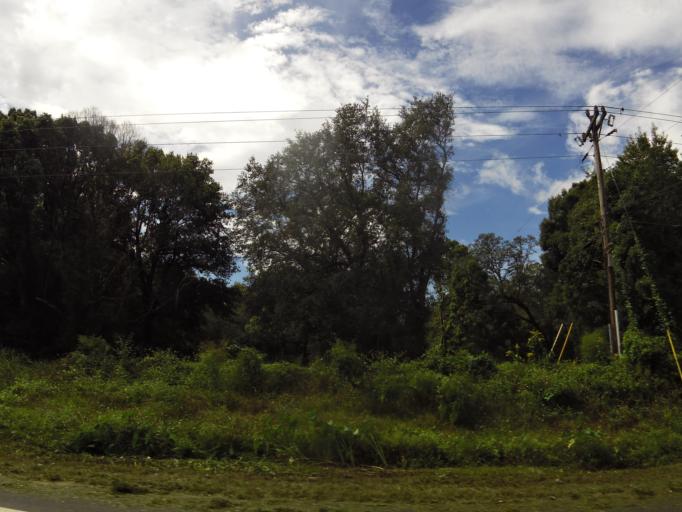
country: US
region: Florida
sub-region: Clay County
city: Middleburg
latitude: 30.1332
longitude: -81.9997
